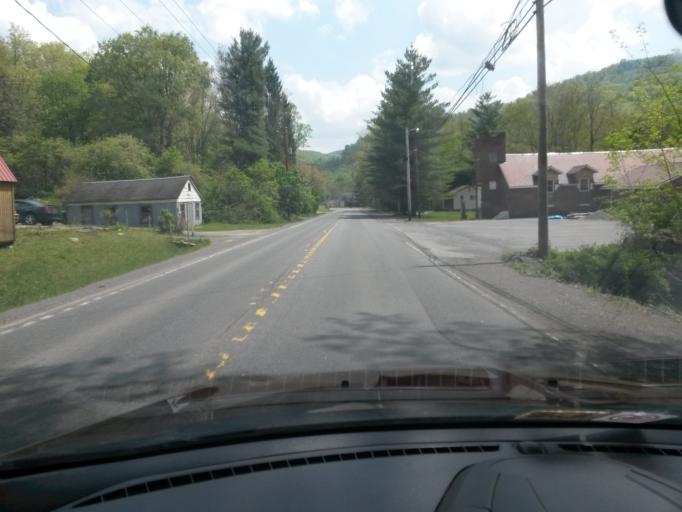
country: US
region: West Virginia
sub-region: Greenbrier County
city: Rainelle
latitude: 37.9925
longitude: -80.7341
